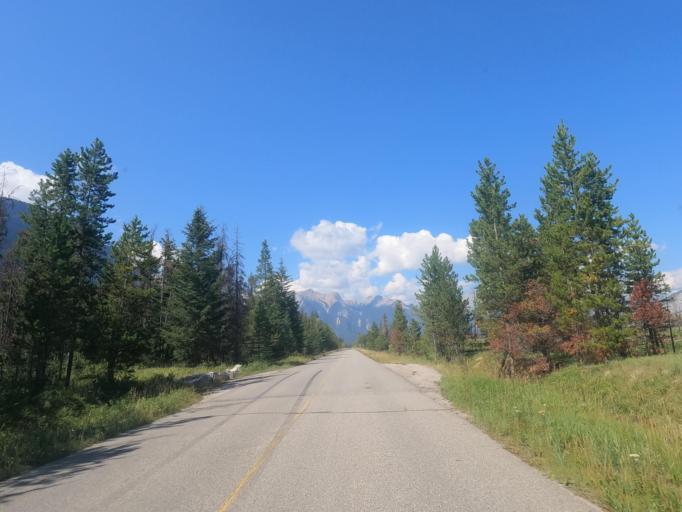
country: CA
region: Alberta
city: Jasper Park Lodge
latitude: 52.9763
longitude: -118.0656
